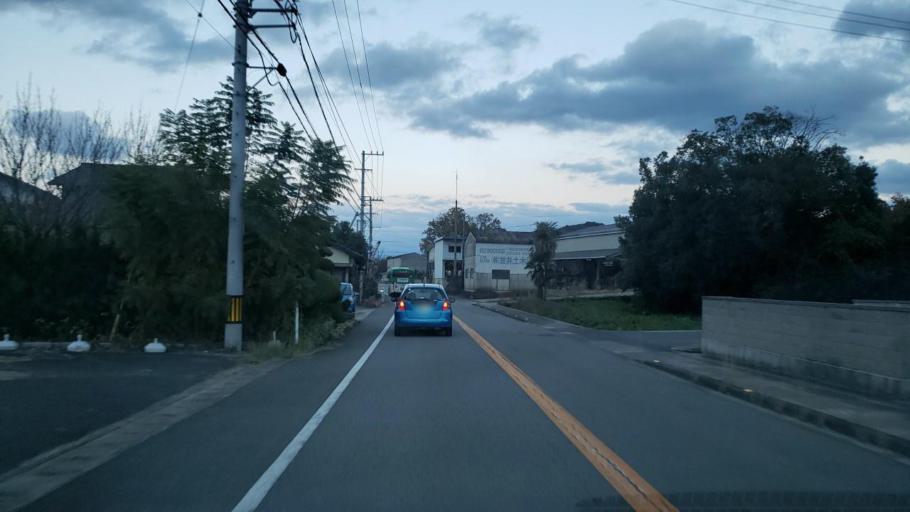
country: JP
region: Tokushima
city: Kamojimacho-jogejima
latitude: 34.2283
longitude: 134.3425
